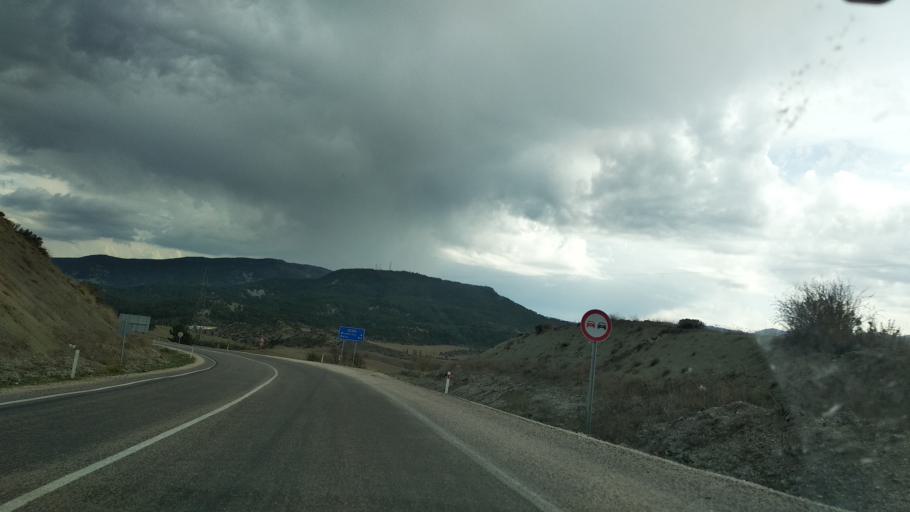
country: TR
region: Bolu
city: Mudurnu
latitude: 40.4783
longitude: 31.1609
